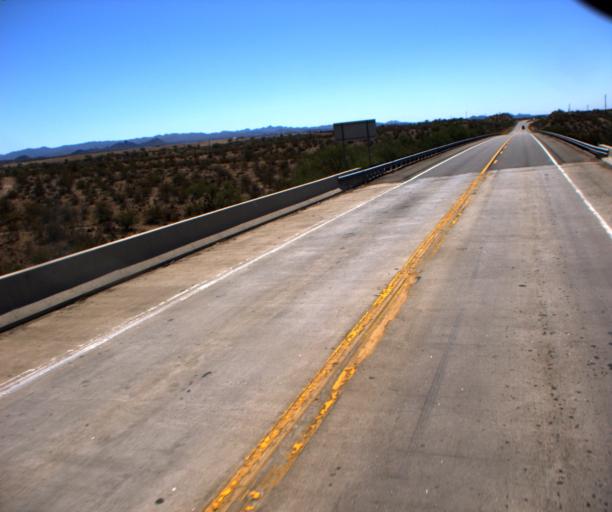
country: US
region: Arizona
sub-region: Maricopa County
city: Wickenburg
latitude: 34.0309
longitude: -112.8174
